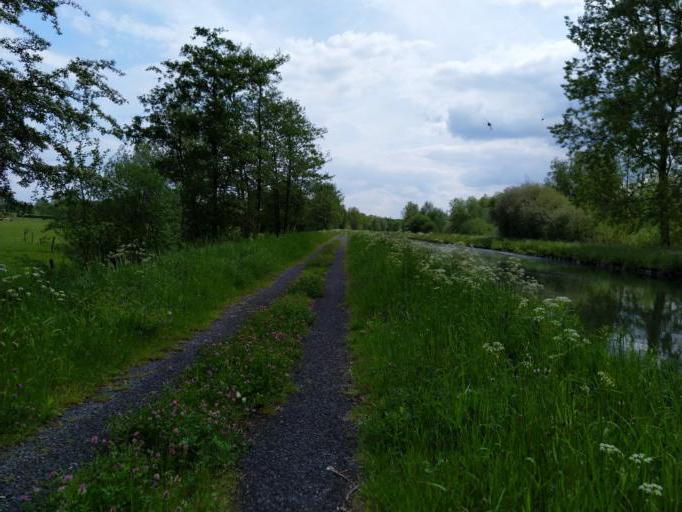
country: FR
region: Picardie
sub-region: Departement de l'Aisne
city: Wassigny
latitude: 50.0653
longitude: 3.6487
